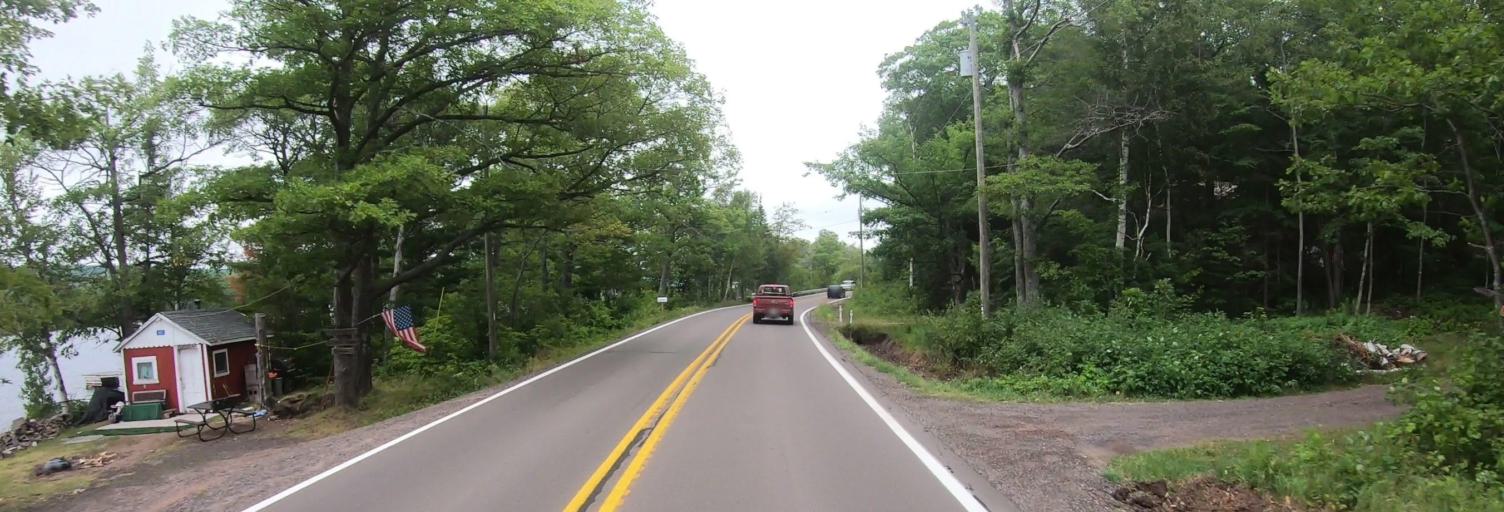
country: US
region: Michigan
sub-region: Keweenaw County
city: Eagle River
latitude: 47.4353
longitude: -87.9712
